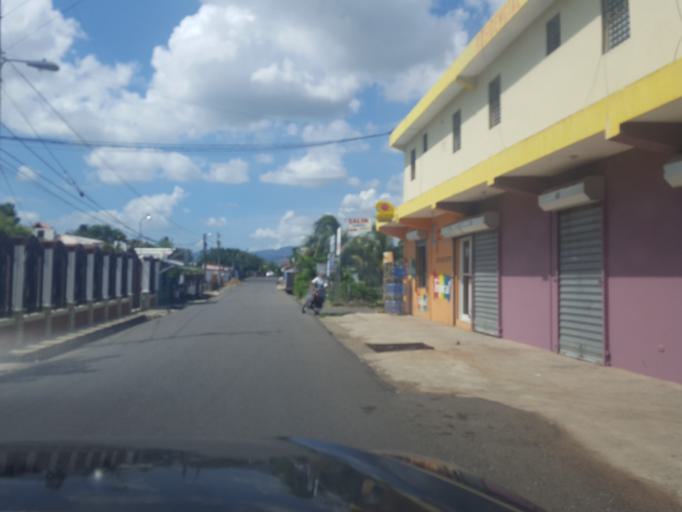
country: DO
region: Santiago
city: Licey al Medio
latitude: 19.3906
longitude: -70.6488
